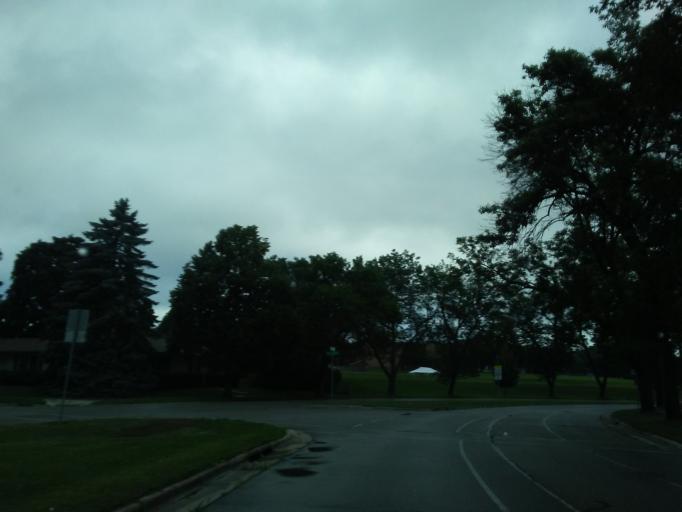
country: US
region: Wisconsin
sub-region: Dane County
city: Shorewood Hills
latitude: 43.0627
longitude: -89.4582
